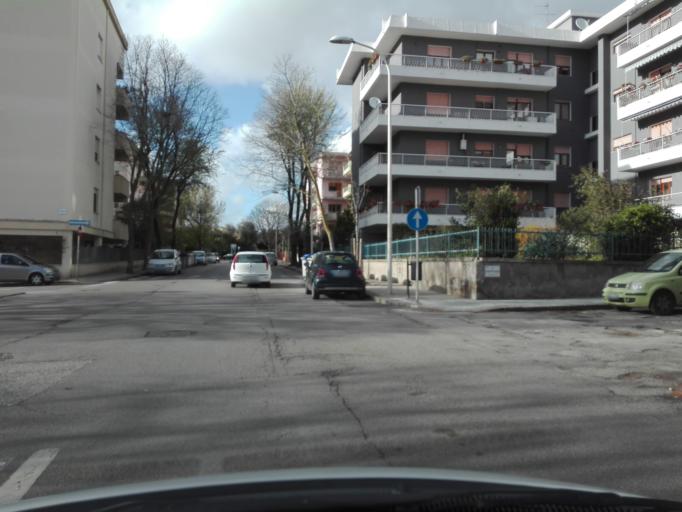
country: IT
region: Sardinia
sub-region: Provincia di Sassari
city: Sassari
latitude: 40.7218
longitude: 8.5816
